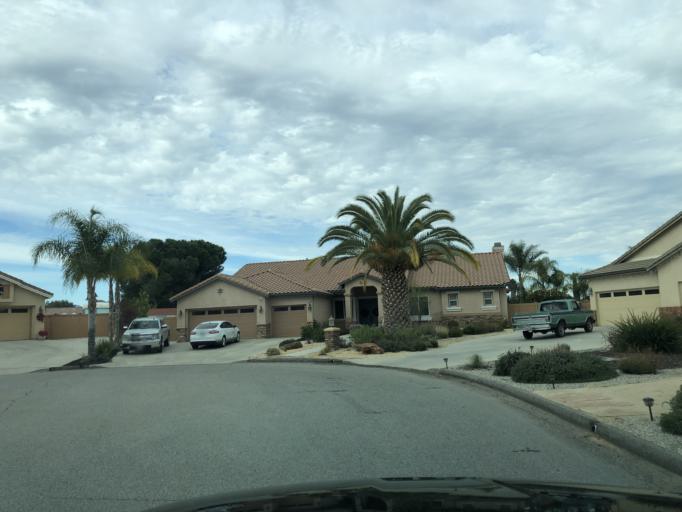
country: US
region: California
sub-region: Riverside County
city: Wildomar
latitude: 33.6026
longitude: -117.2843
